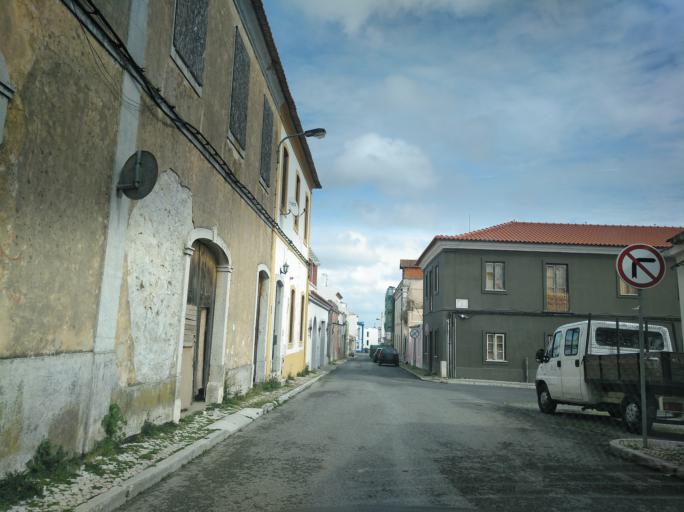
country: PT
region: Setubal
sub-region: Grandola
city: Grandola
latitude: 38.1741
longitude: -8.5681
